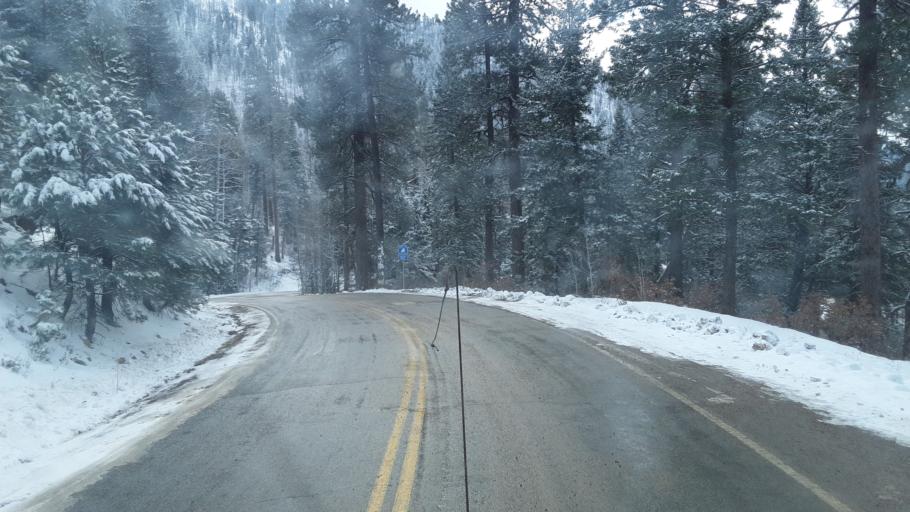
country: US
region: Colorado
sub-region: La Plata County
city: Bayfield
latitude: 37.3799
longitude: -107.6591
